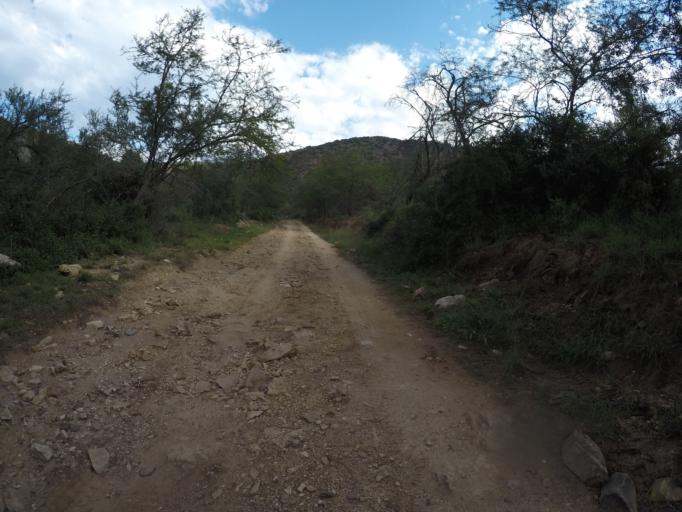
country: ZA
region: Eastern Cape
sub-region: Cacadu District Municipality
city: Kareedouw
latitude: -33.6366
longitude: 24.3171
